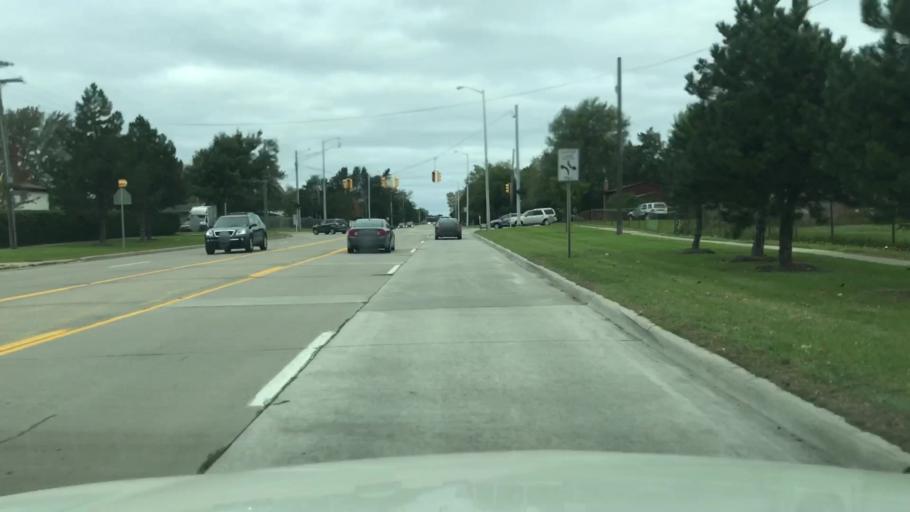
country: US
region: Michigan
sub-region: Macomb County
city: Sterling Heights
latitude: 42.5576
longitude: -83.0695
